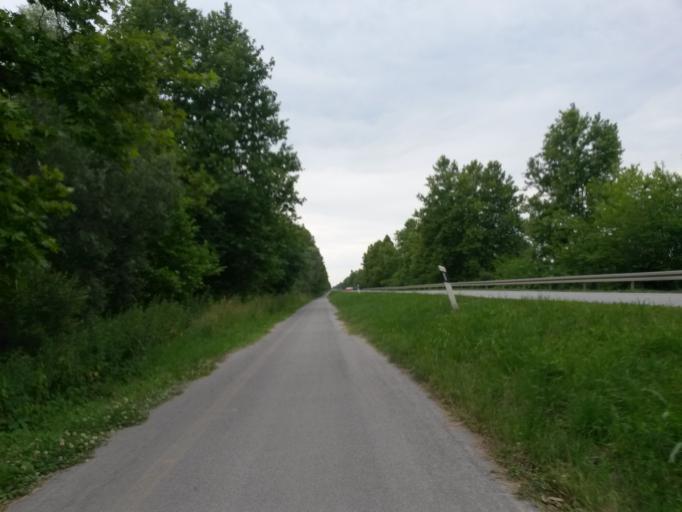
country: HR
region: Osjecko-Baranjska
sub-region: Grad Osijek
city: Bilje
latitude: 45.5902
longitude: 18.7353
